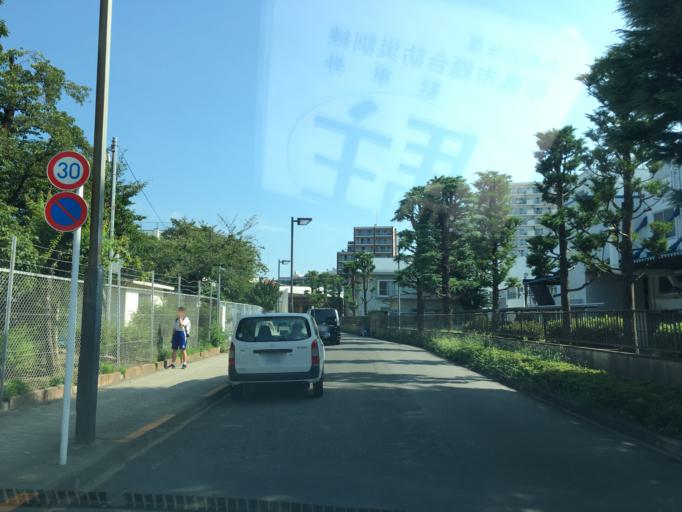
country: JP
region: Tokyo
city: Fussa
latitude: 35.7159
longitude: 139.3445
